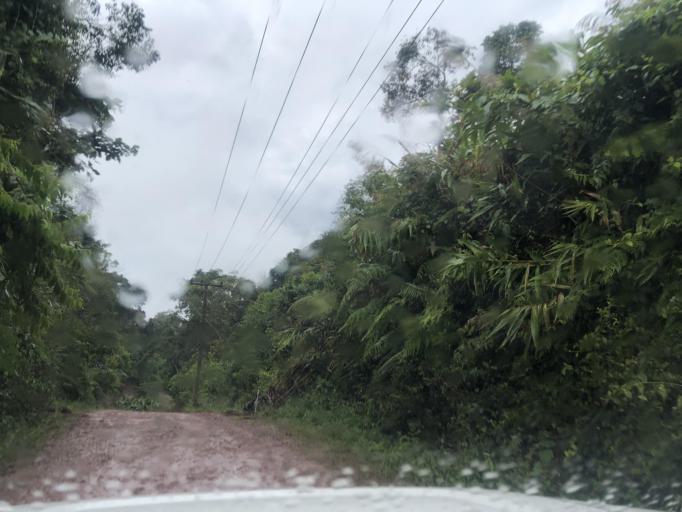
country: LA
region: Oudomxai
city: Muang La
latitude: 21.2302
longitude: 101.9833
